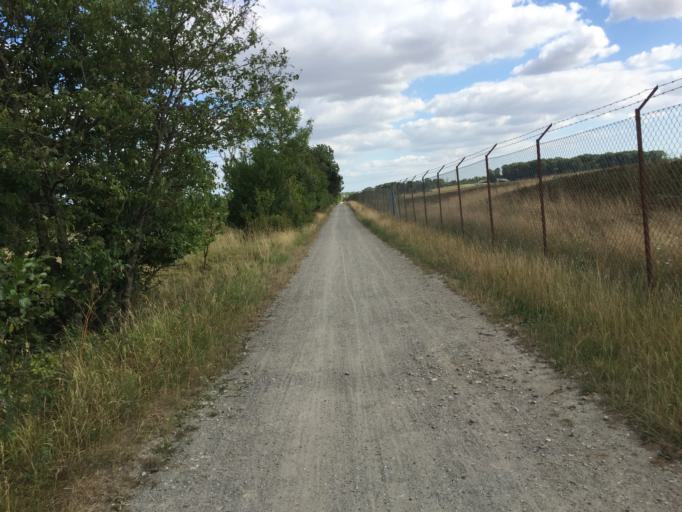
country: DK
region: South Denmark
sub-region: Odense Kommune
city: Neder Holluf
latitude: 55.3644
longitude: 10.4315
